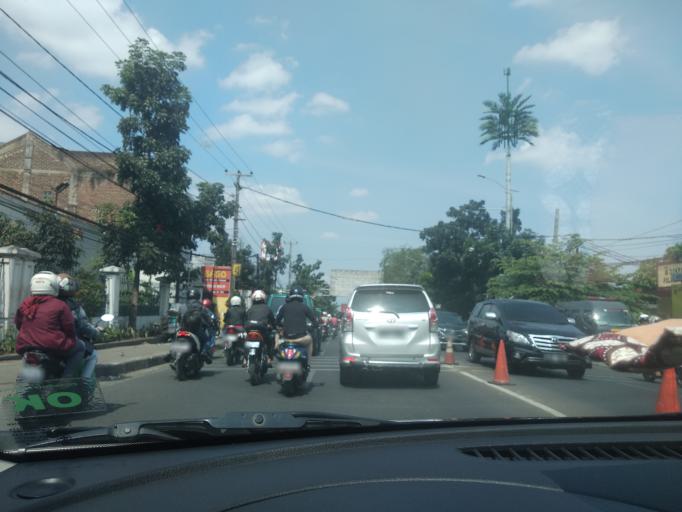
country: ID
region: West Java
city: Cimahi
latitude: -6.8854
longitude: 107.5539
